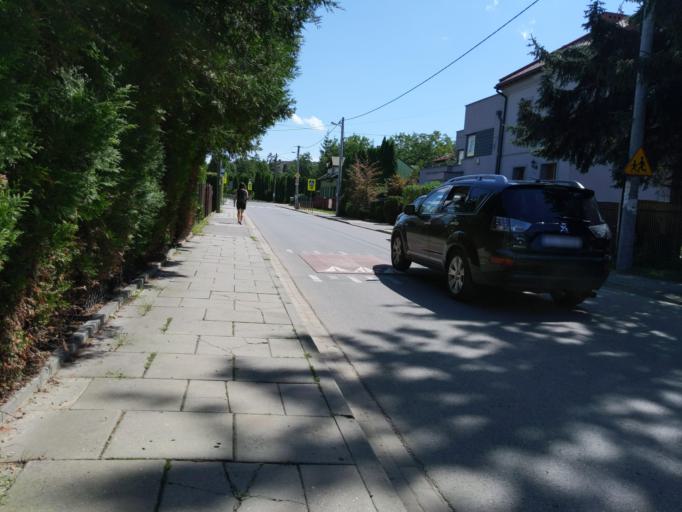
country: PL
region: Lesser Poland Voivodeship
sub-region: Krakow
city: Krakow
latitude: 50.0376
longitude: 19.9912
